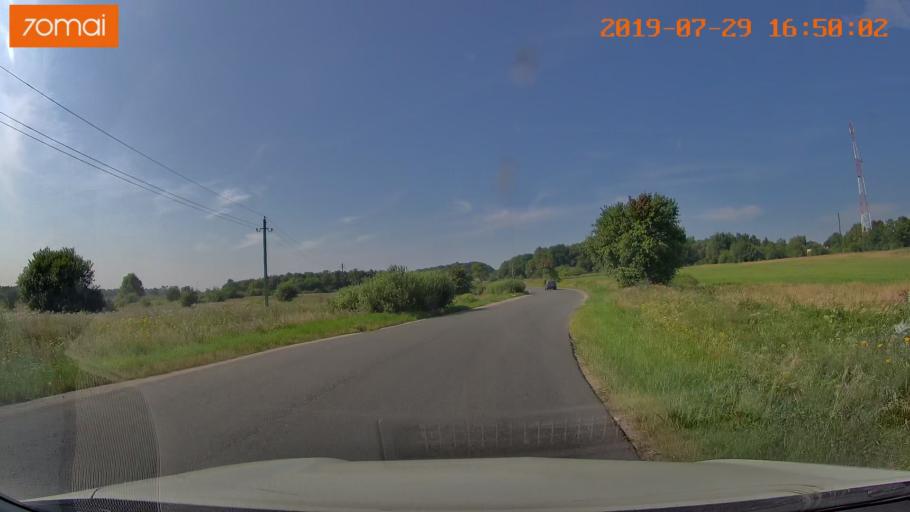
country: RU
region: Kaliningrad
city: Primorsk
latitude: 54.7995
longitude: 20.0584
